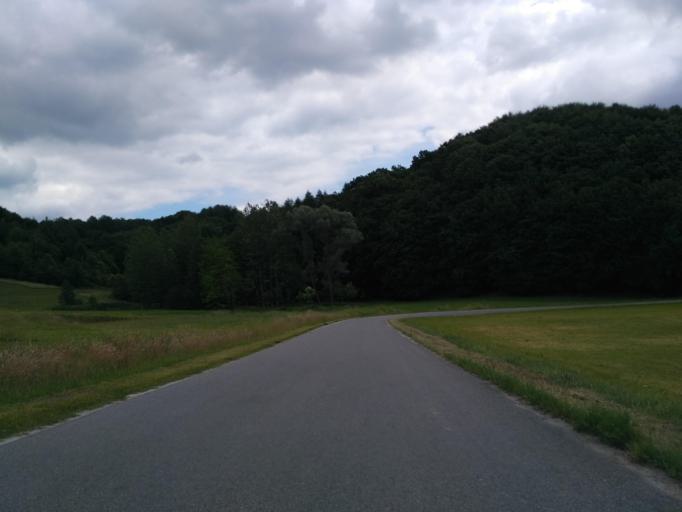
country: PL
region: Subcarpathian Voivodeship
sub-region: Powiat przeworski
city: Jawornik Polski
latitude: 49.8513
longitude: 22.3022
